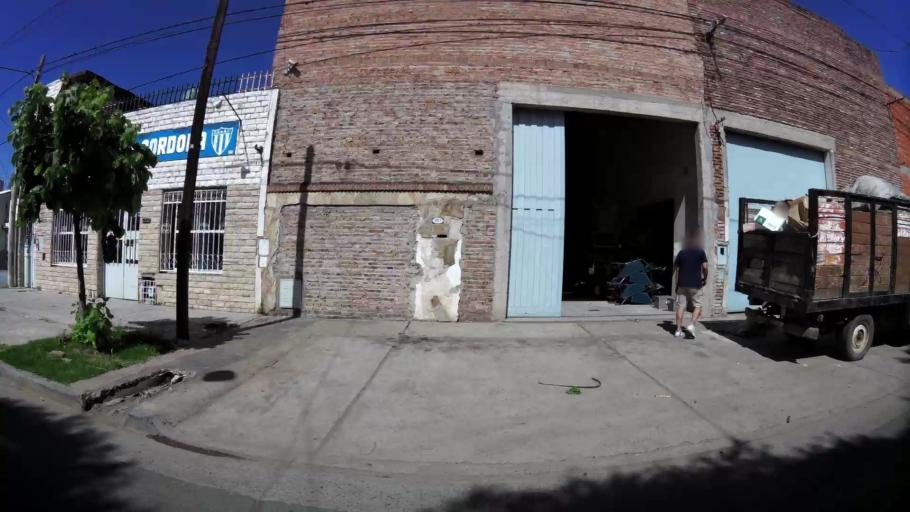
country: AR
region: Santa Fe
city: Granadero Baigorria
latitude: -32.9343
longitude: -60.7187
